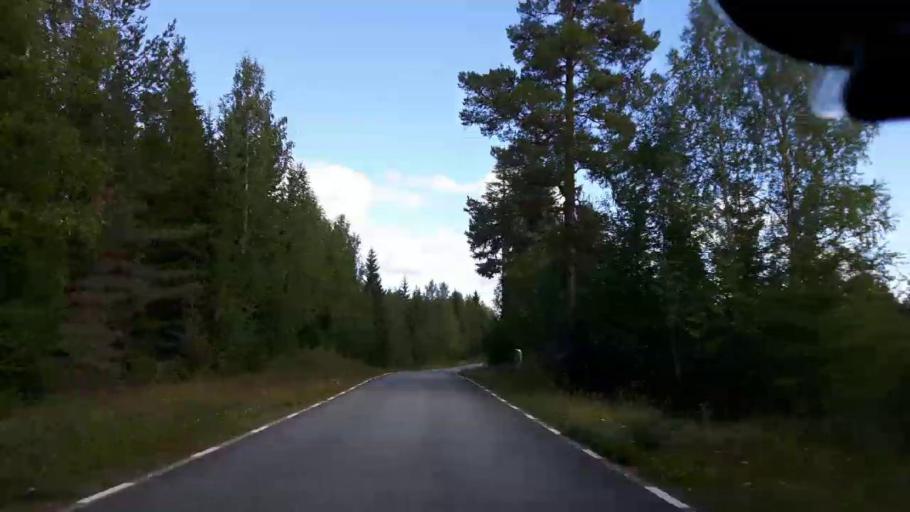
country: SE
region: Jaemtland
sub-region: OEstersunds Kommun
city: Brunflo
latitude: 63.2000
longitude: 15.2254
